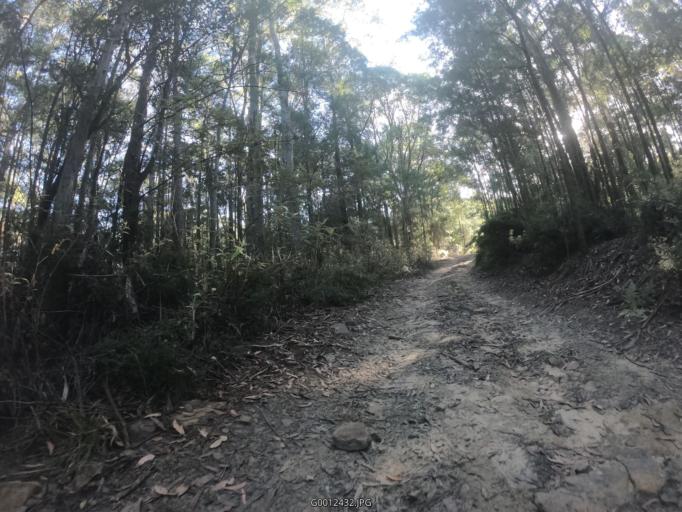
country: AU
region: New South Wales
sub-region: Lake Macquarie Shire
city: Cooranbong
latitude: -33.0857
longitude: 151.3612
